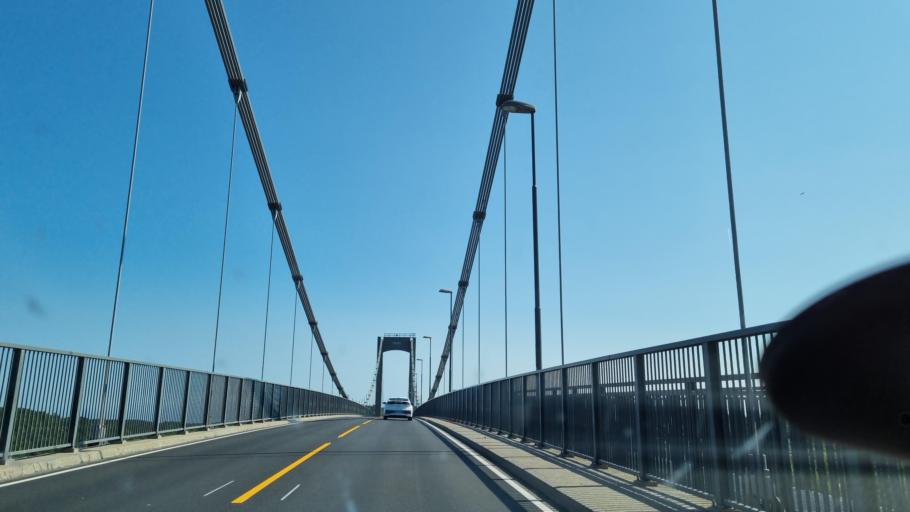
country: NO
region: Aust-Agder
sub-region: Arendal
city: Arendal
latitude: 58.4721
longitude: 8.8224
